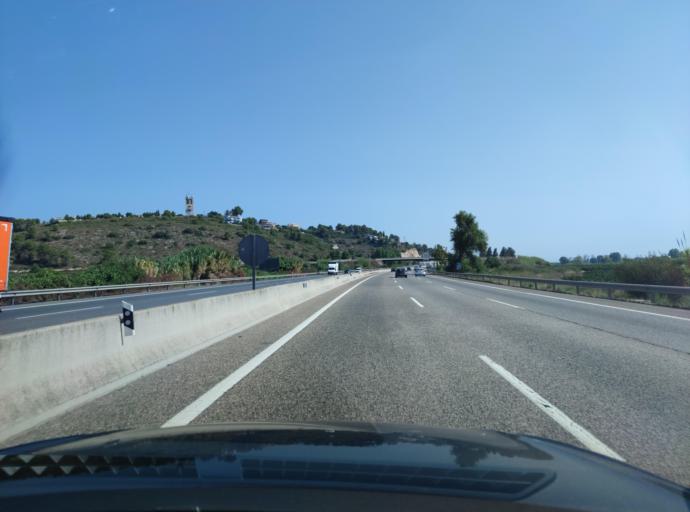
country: ES
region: Valencia
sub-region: Provincia de Valencia
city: Gavarda
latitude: 39.0834
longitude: -0.5406
